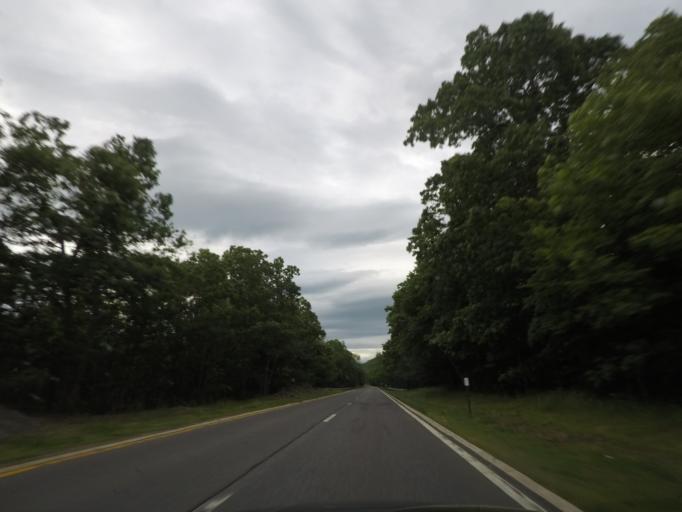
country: US
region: New York
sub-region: Dutchess County
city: Pine Plains
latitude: 42.0506
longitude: -73.7325
